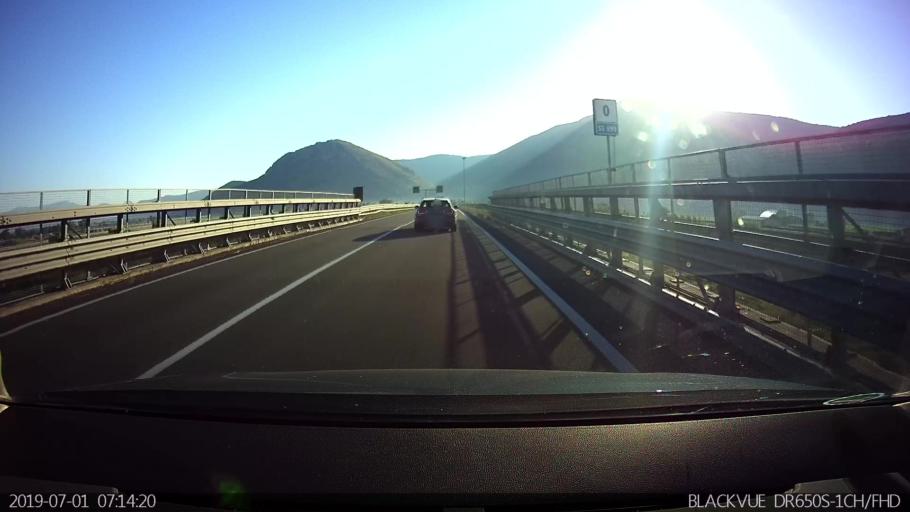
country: IT
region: Latium
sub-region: Provincia di Latina
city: Borgo Hermada
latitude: 41.3215
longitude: 13.1836
